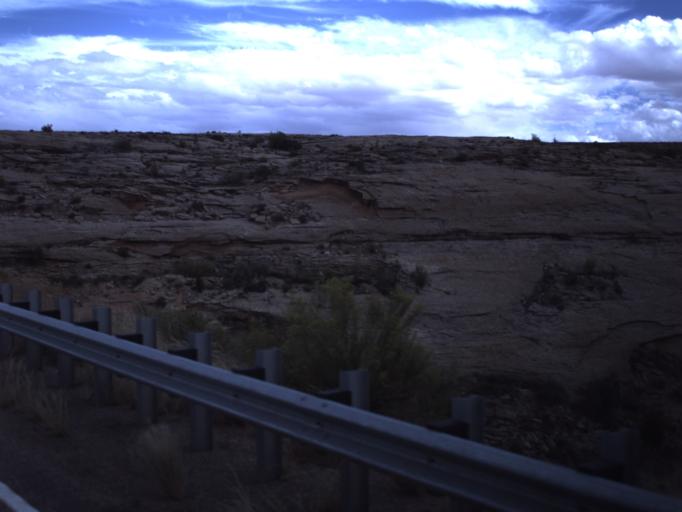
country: US
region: Utah
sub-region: San Juan County
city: Blanding
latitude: 37.2638
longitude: -109.6529
